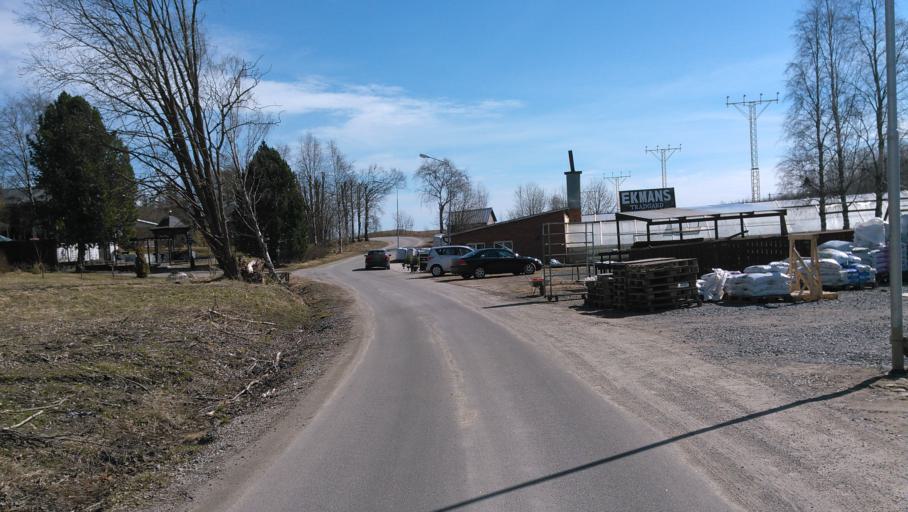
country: SE
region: Vaesterbotten
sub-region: Umea Kommun
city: Umea
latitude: 63.8044
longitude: 20.2583
